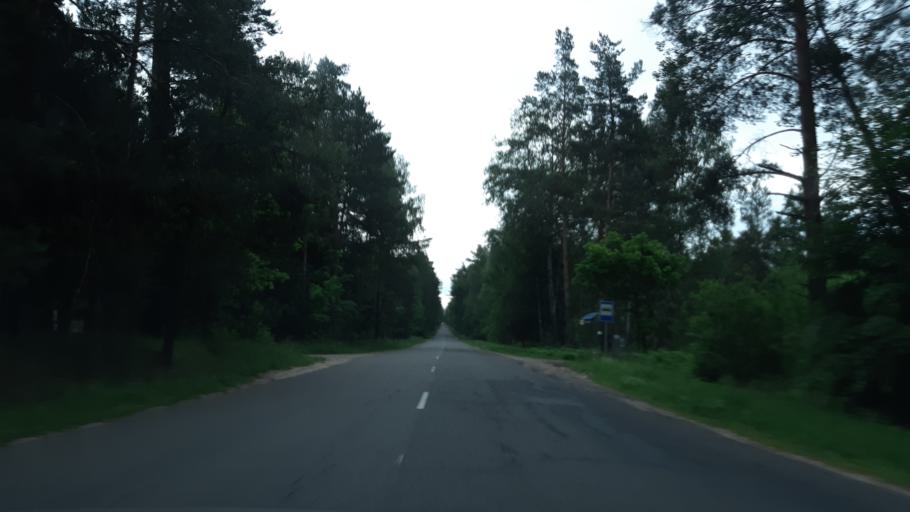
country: BY
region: Minsk
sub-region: Smalyavitski Rayon
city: Oktjabr'skij
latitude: 54.1112
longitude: 28.1993
